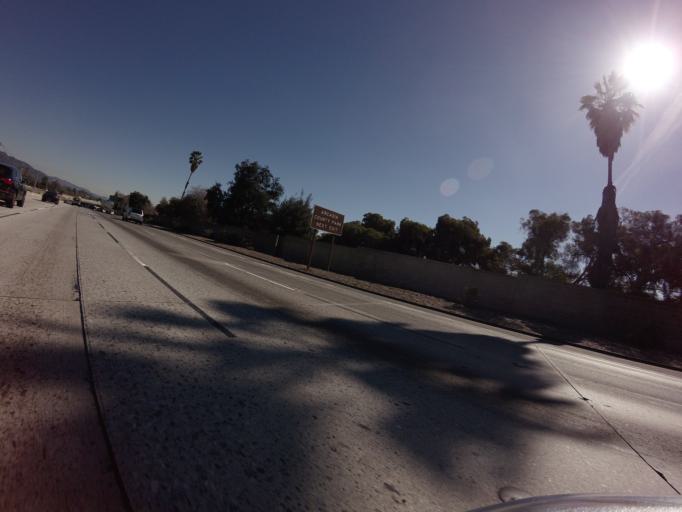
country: US
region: California
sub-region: Los Angeles County
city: Bradbury
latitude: 34.1333
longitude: -117.9540
